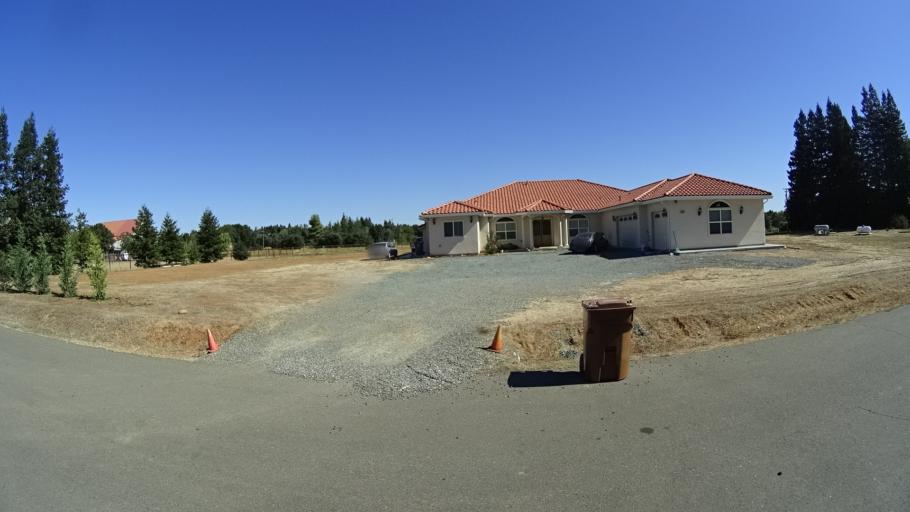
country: US
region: California
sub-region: Sacramento County
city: Wilton
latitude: 38.4195
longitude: -121.3049
